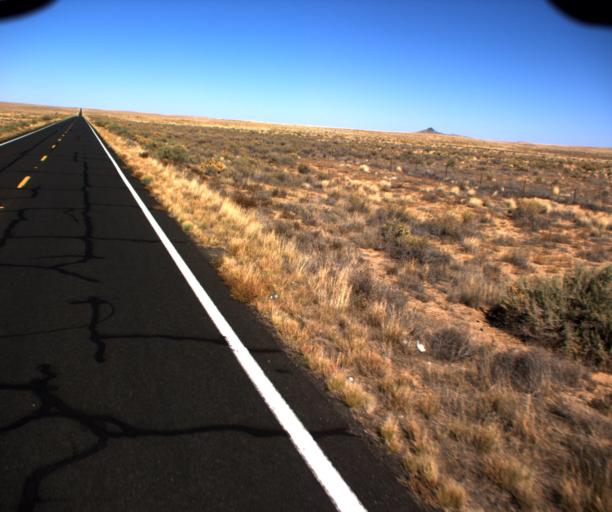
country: US
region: Arizona
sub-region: Navajo County
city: Dilkon
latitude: 35.5792
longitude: -110.4632
